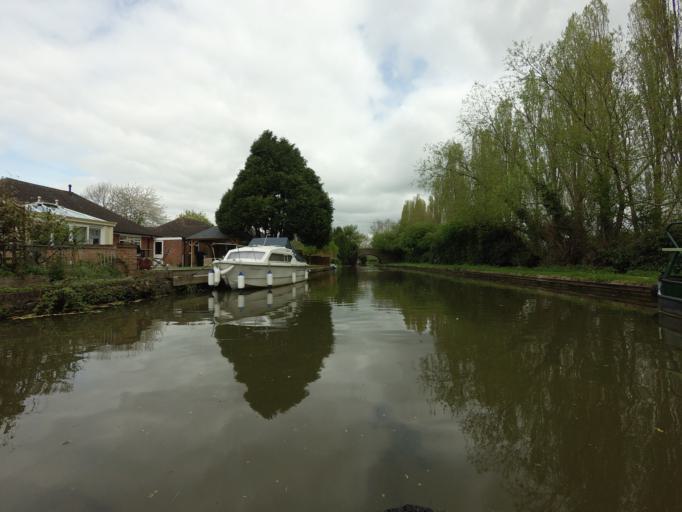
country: GB
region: England
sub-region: Milton Keynes
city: Water Eaton
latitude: 51.9874
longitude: -0.7175
